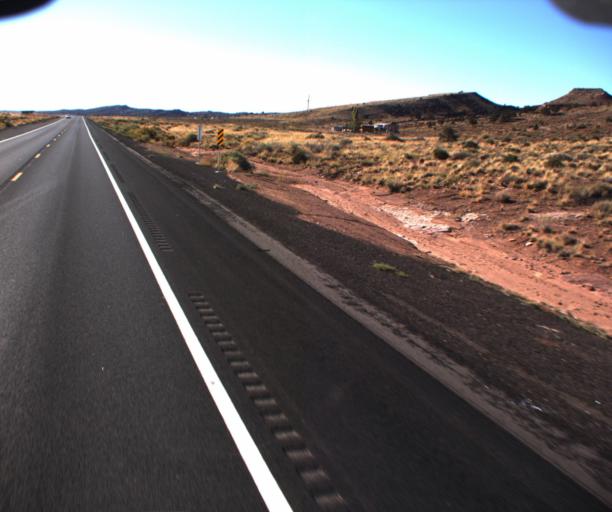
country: US
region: Arizona
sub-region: Coconino County
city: LeChee
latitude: 36.4787
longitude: -111.5733
